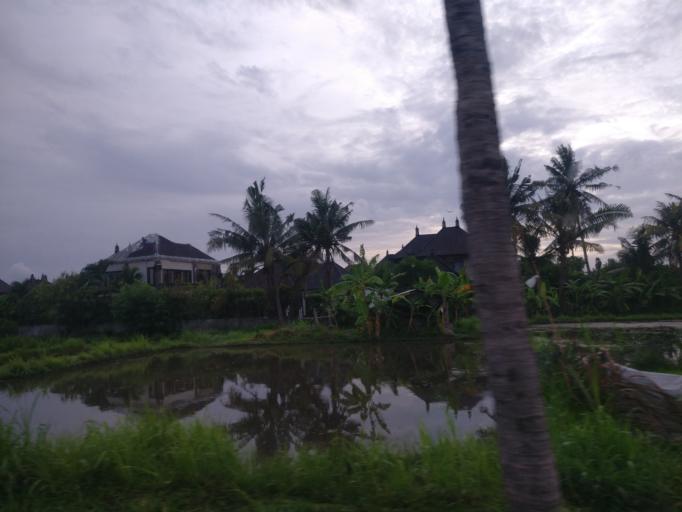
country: ID
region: Bali
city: Banjar Pasekan
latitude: -8.5969
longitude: 115.3362
